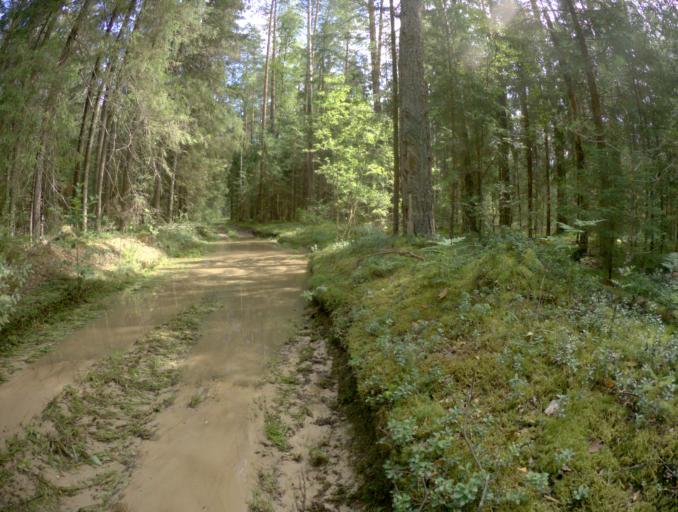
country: RU
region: Vladimir
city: Orgtrud
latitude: 56.0766
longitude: 40.6107
